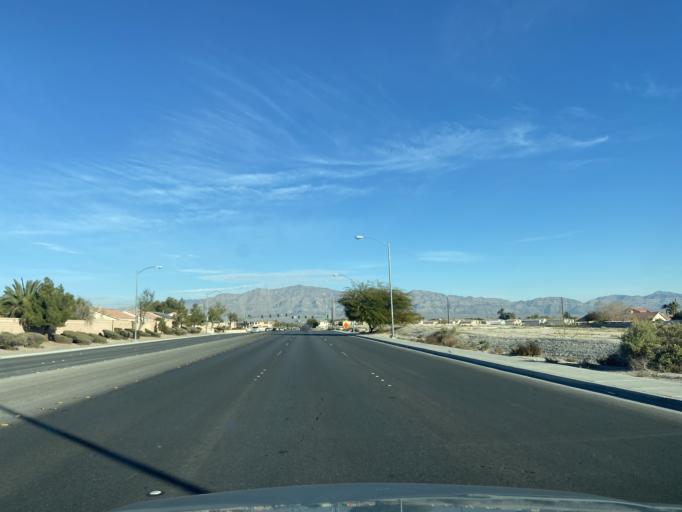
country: US
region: Nevada
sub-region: Clark County
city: North Las Vegas
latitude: 36.2446
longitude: -115.1800
